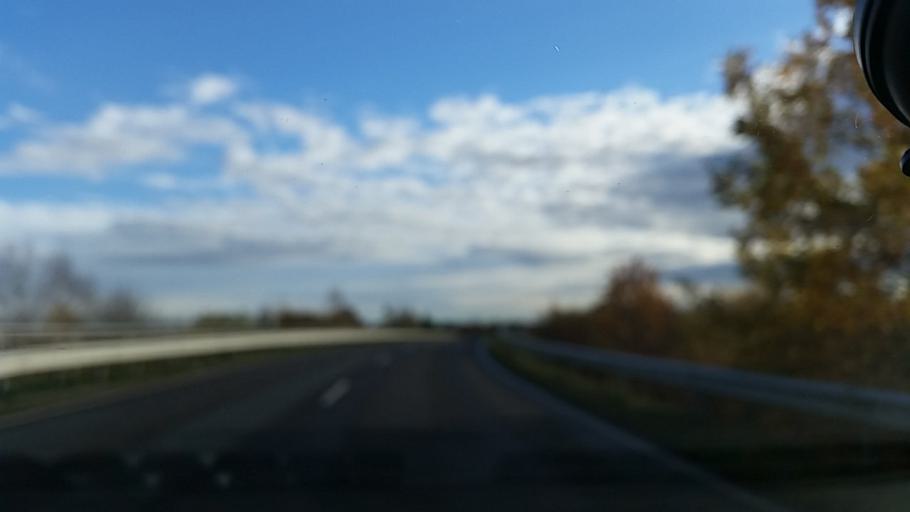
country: DE
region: Lower Saxony
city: Danndorf
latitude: 52.4320
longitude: 10.8690
